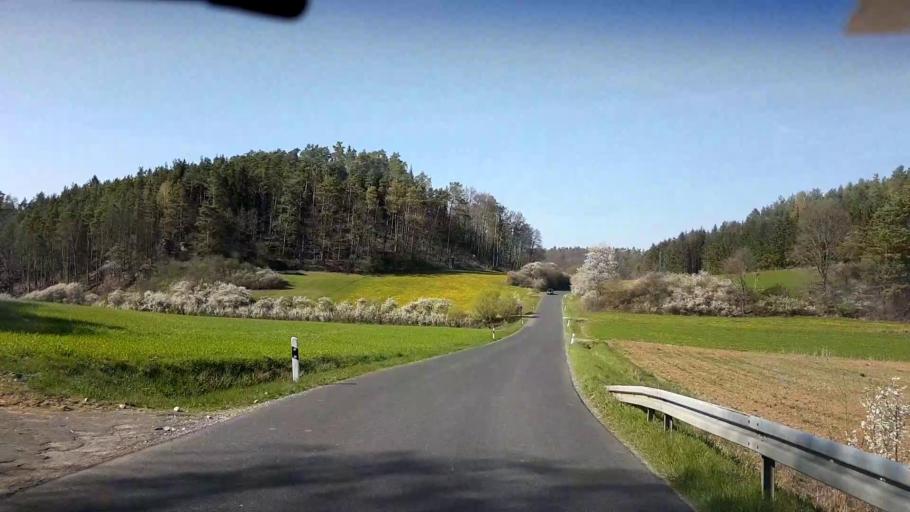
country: DE
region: Bavaria
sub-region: Upper Franconia
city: Waischenfeld
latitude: 49.8316
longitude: 11.3509
